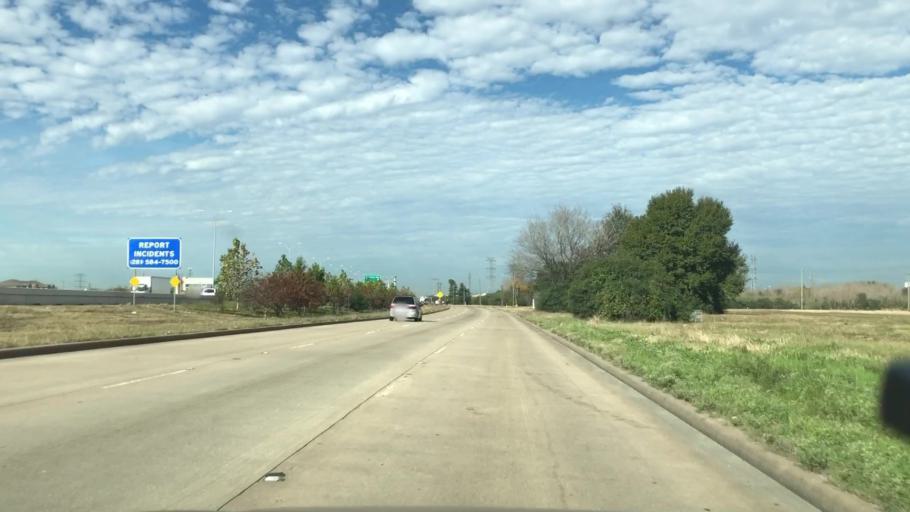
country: US
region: Texas
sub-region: Fort Bend County
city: Missouri City
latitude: 29.6183
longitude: -95.5021
